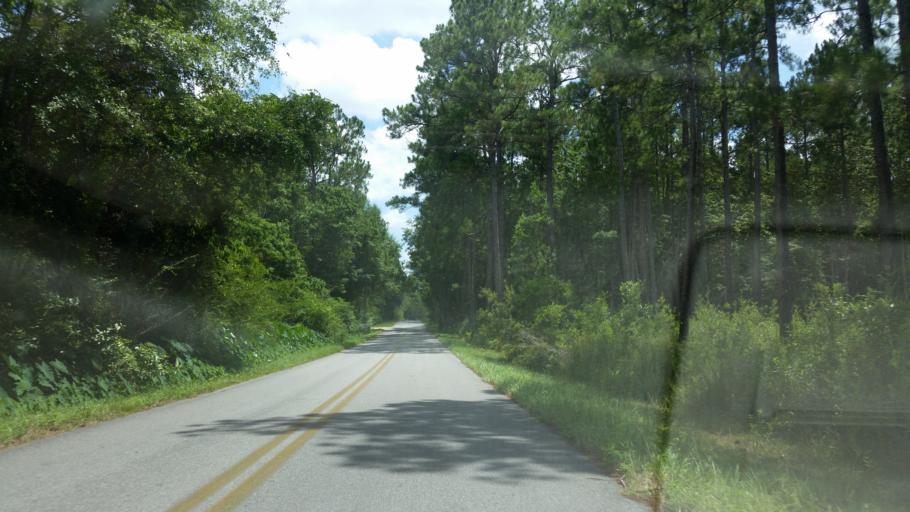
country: US
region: Florida
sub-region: Santa Rosa County
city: Point Baker
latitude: 30.7272
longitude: -86.8751
